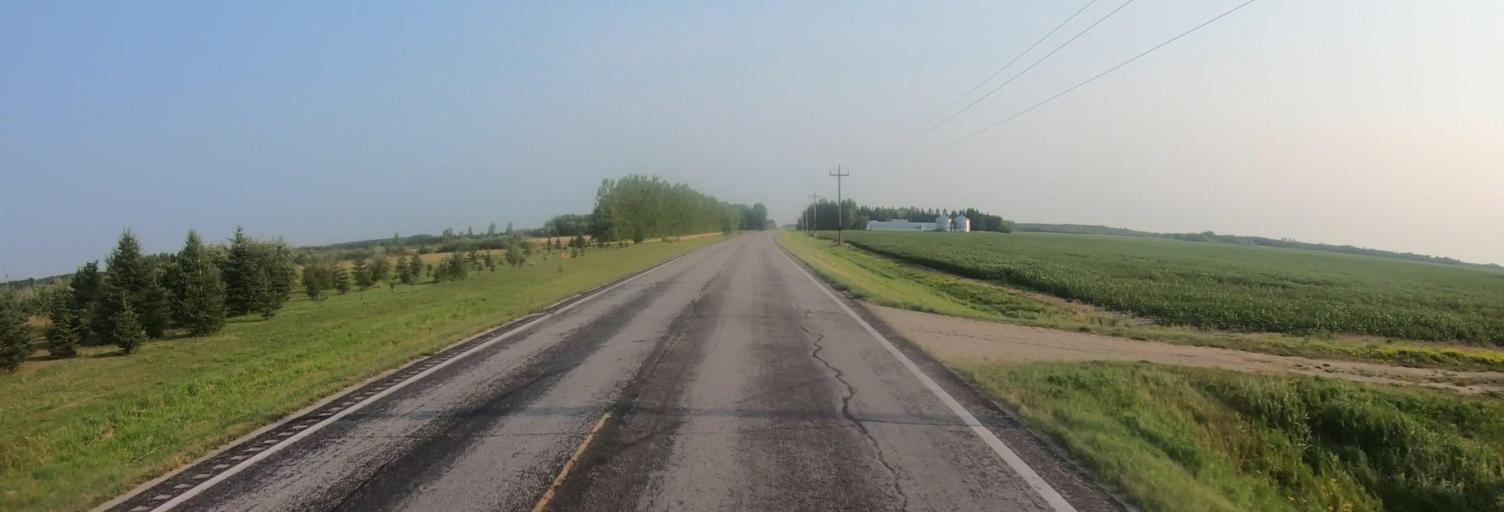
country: US
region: Minnesota
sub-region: Roseau County
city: Warroad
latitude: 48.7913
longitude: -95.3307
